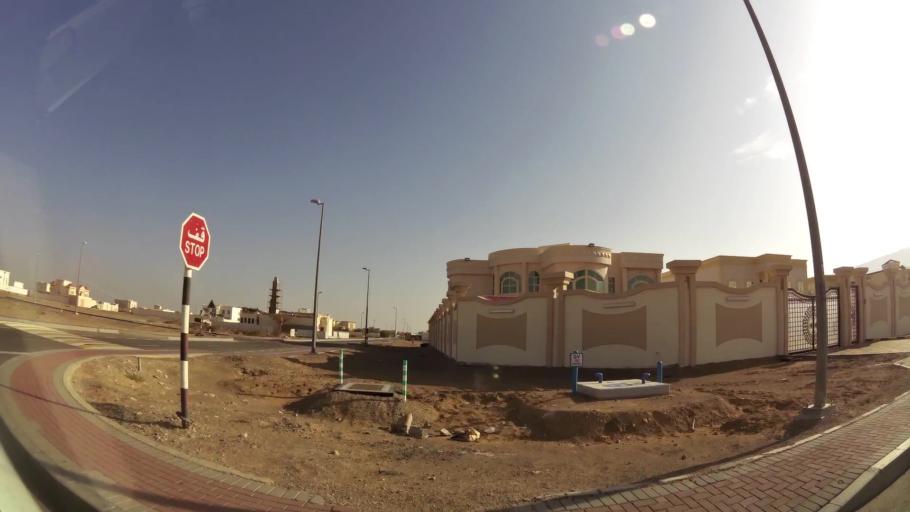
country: AE
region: Abu Dhabi
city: Al Ain
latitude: 24.0515
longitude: 55.8453
